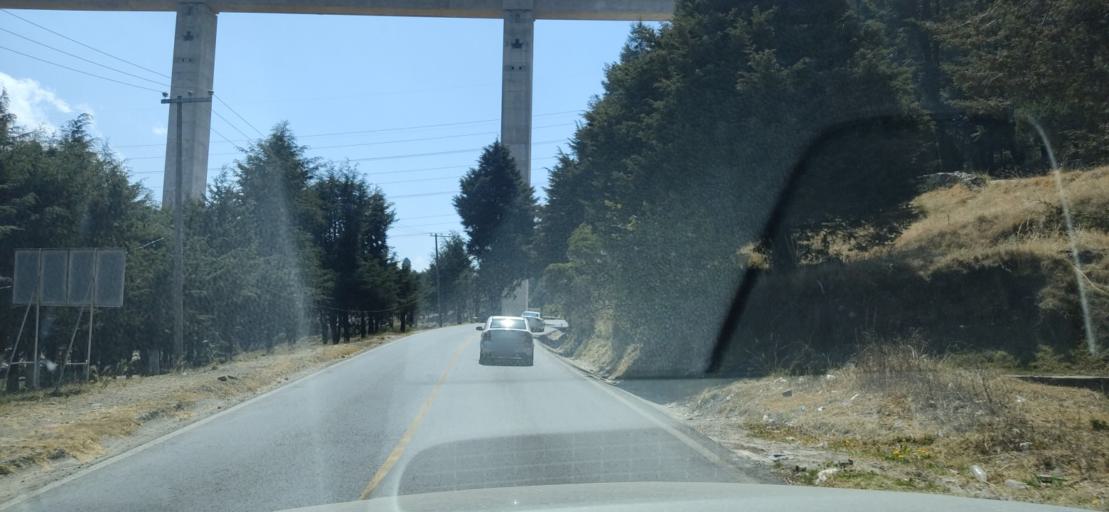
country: MX
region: Morelos
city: San Jeronimo Acazulco
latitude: 19.2959
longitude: -99.3752
